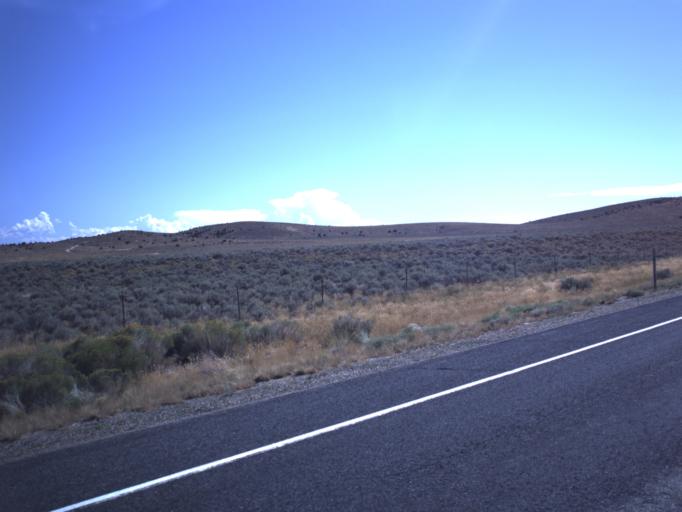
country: US
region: Utah
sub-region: Utah County
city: Eagle Mountain
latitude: 40.0767
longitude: -112.3904
